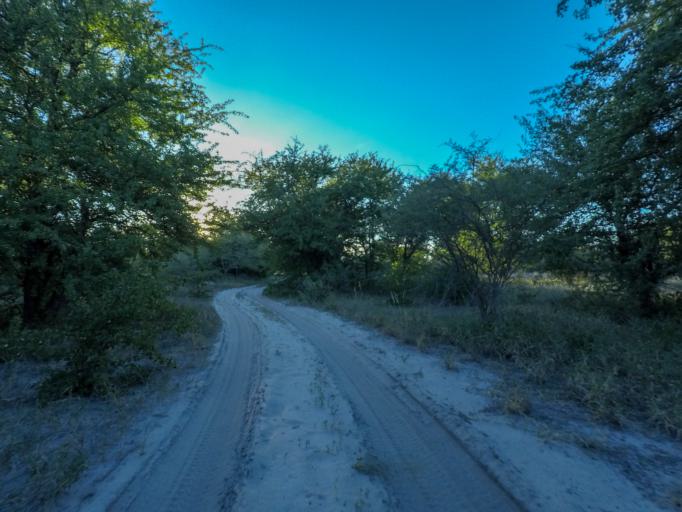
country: BW
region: Central
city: Rakops
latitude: -21.4036
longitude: 23.7738
